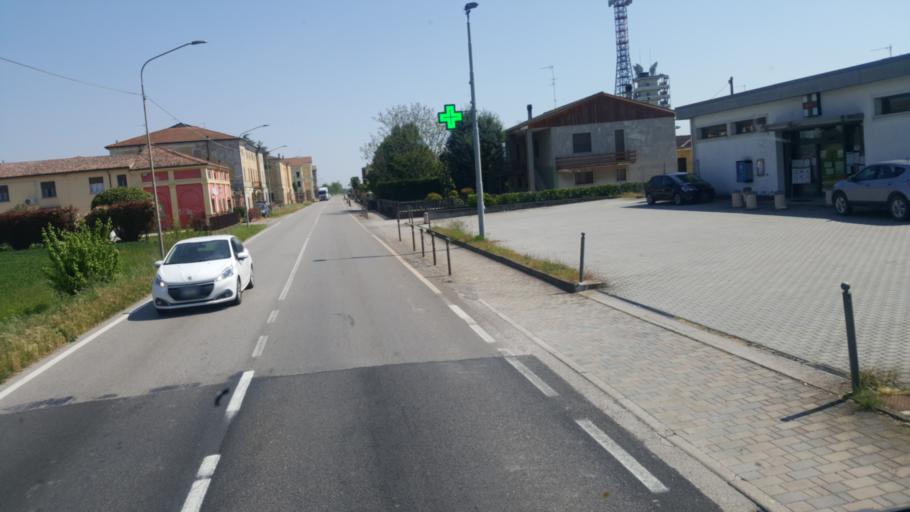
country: IT
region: Lombardy
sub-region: Provincia di Mantova
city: Serravalle a Po
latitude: 45.0652
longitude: 11.0787
